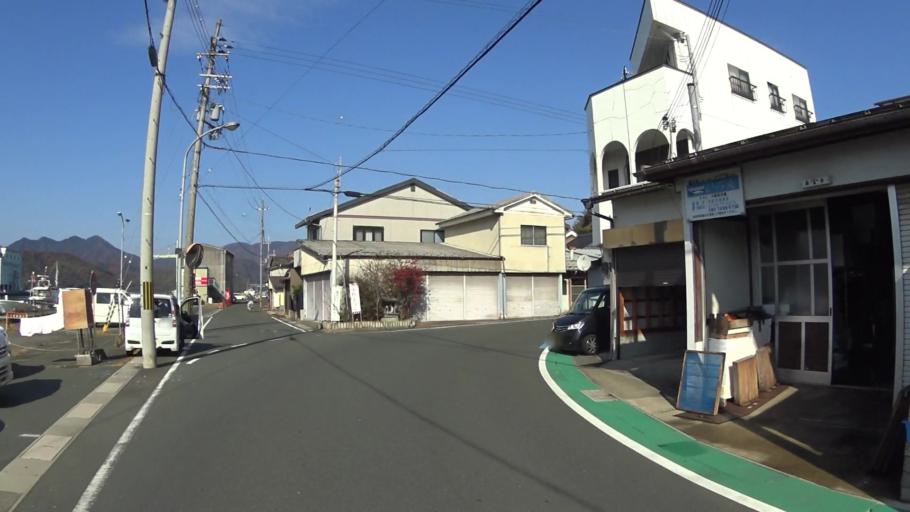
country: JP
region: Kyoto
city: Maizuru
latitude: 35.4569
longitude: 135.3276
